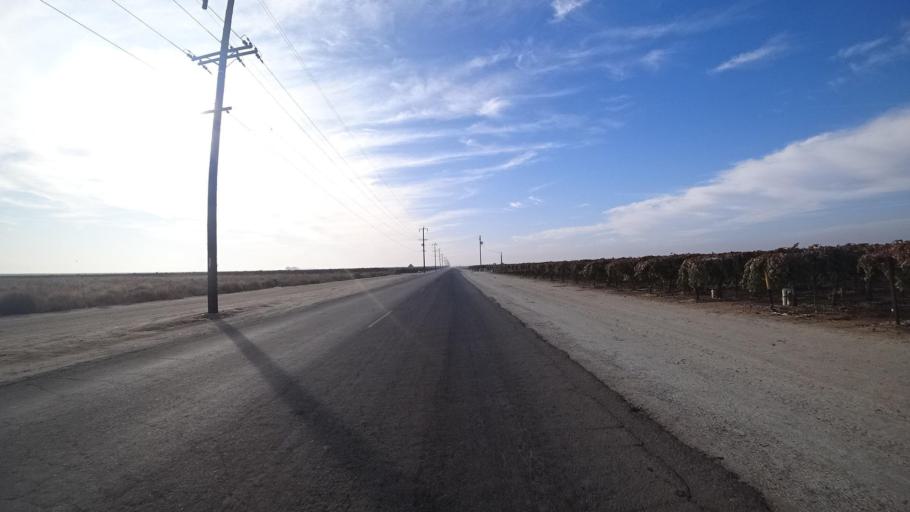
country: US
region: California
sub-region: Kern County
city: Delano
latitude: 35.7406
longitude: -119.2052
